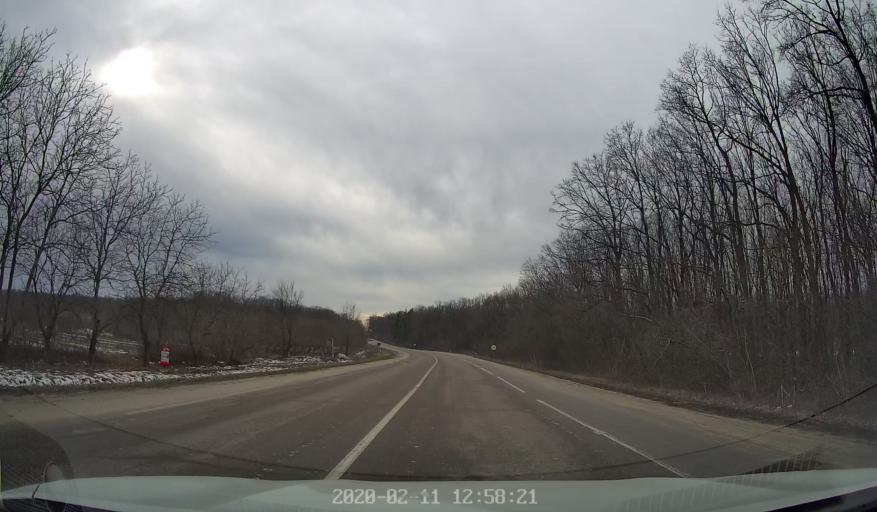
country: MD
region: Briceni
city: Briceni
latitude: 48.3359
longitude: 27.0539
